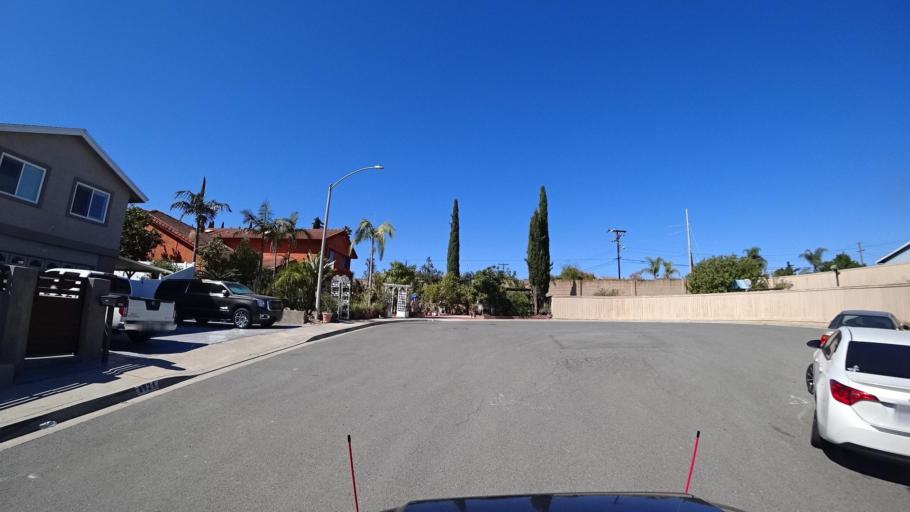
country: US
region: California
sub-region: San Diego County
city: La Presa
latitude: 32.6977
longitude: -117.0056
